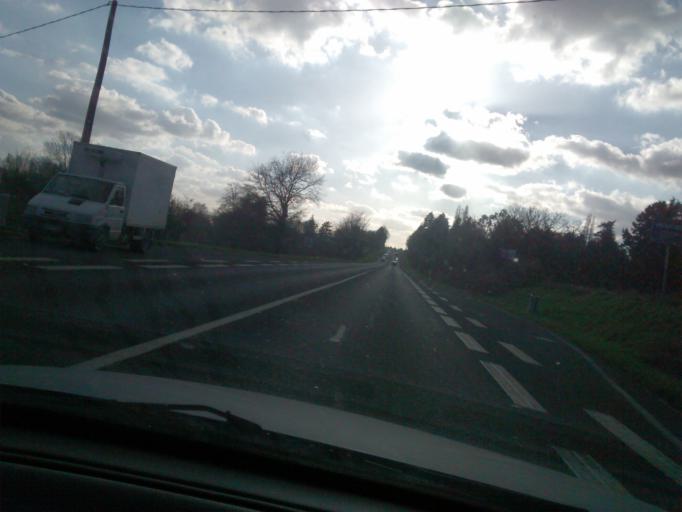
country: FR
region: Pays de la Loire
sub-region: Departement de la Sarthe
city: Change
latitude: 48.0112
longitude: 0.2689
